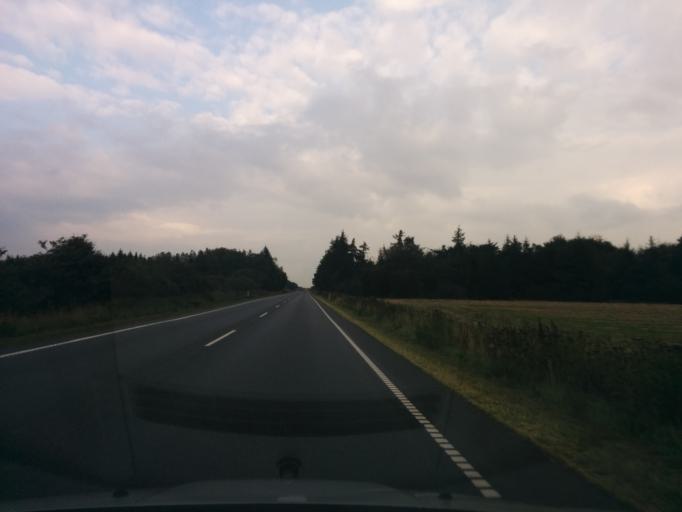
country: DK
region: South Denmark
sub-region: Esbjerg Kommune
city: Bramming
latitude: 55.5953
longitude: 8.7187
